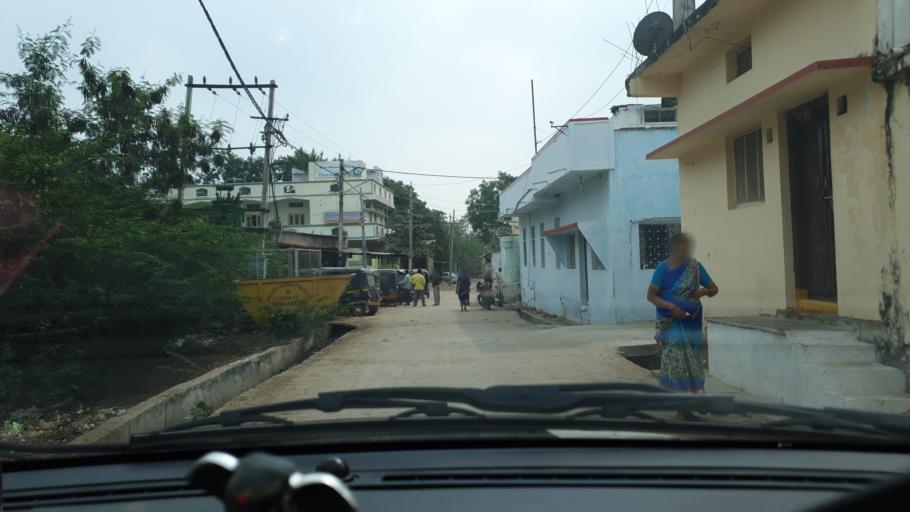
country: IN
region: Karnataka
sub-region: Yadgir
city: Gurmatkal
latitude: 16.8607
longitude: 77.3928
